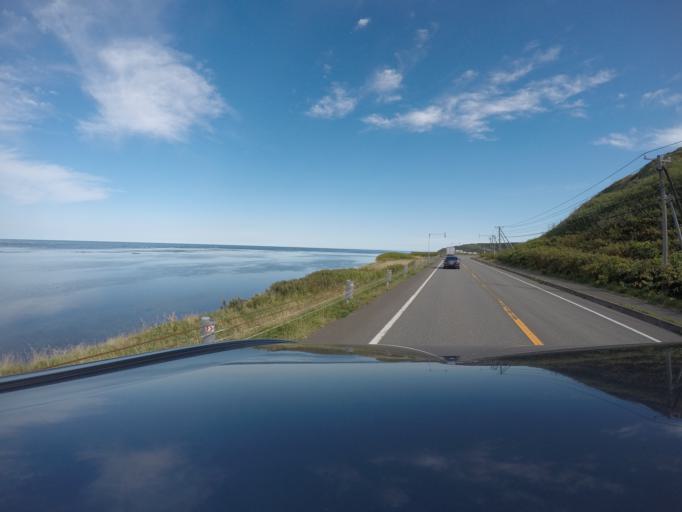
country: JP
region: Hokkaido
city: Makubetsu
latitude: 45.4761
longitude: 141.8748
